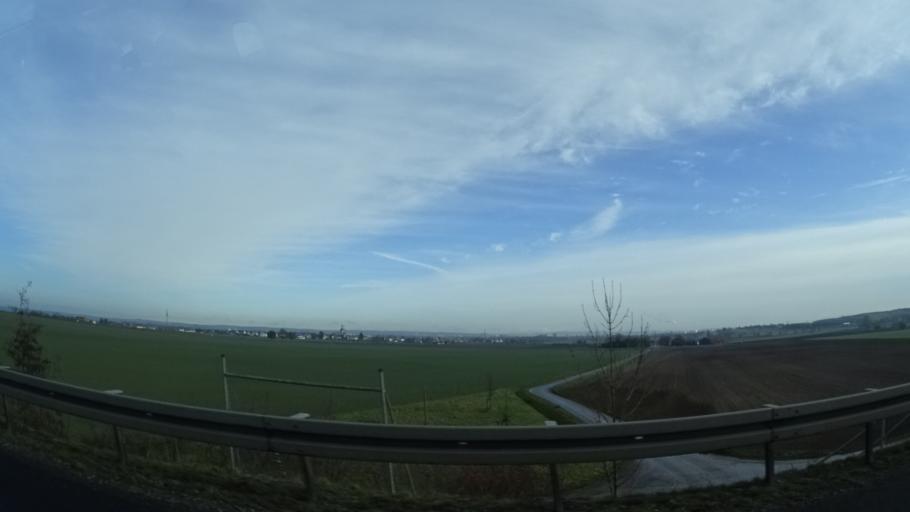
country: DE
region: Bavaria
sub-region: Regierungsbezirk Unterfranken
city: Geldersheim
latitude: 50.0347
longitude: 10.1377
